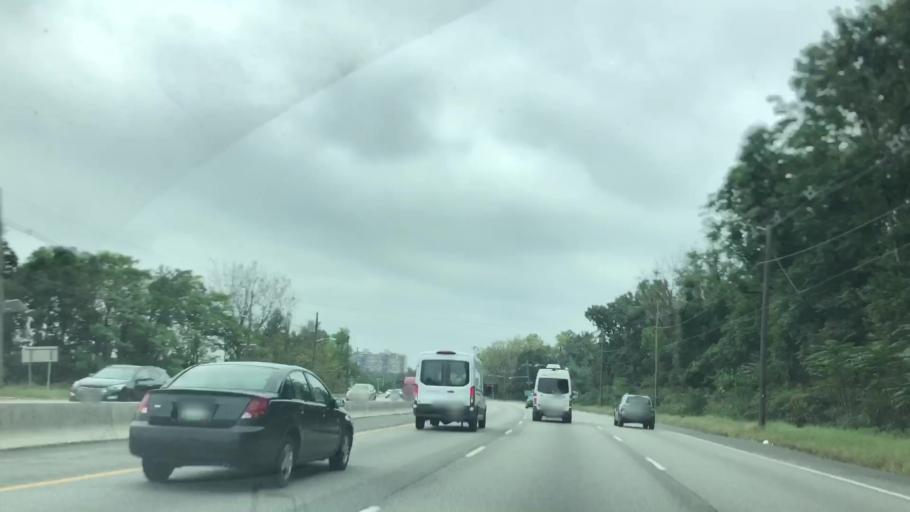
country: US
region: New Jersey
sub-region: Passaic County
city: Clifton
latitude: 40.8599
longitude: -74.1807
